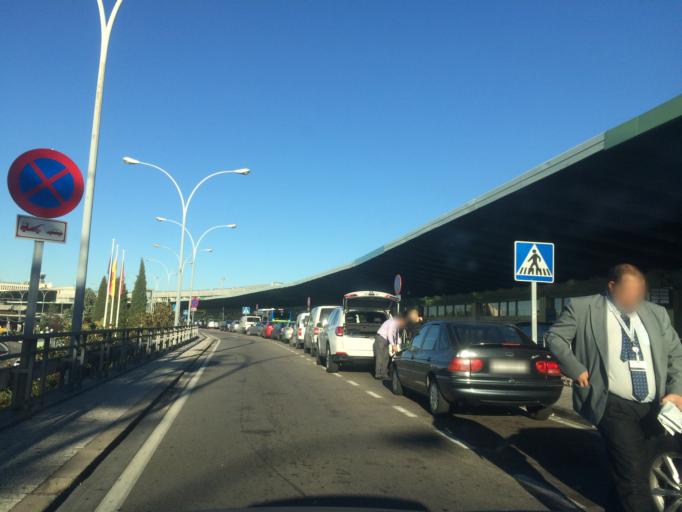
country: ES
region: Madrid
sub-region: Provincia de Madrid
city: Barajas de Madrid
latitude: 40.4630
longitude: -3.5715
